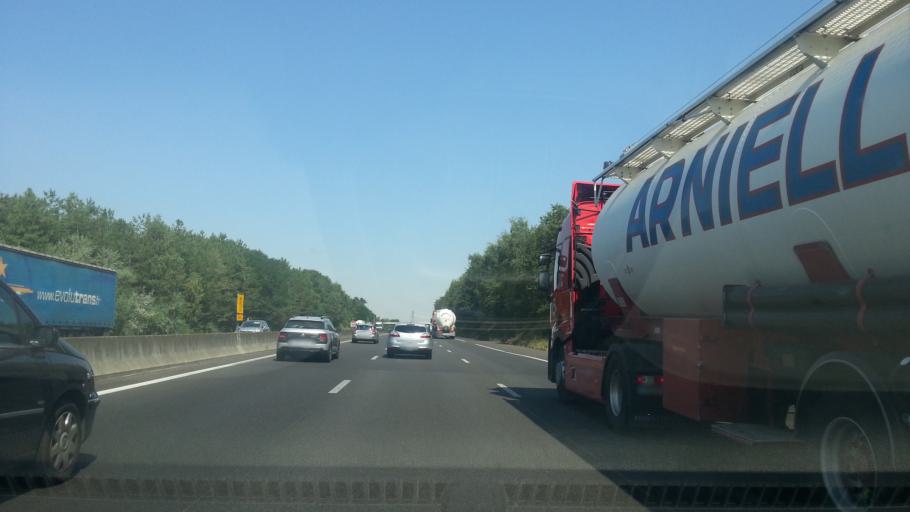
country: FR
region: Centre
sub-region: Departement du Loiret
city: Ingre
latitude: 47.9349
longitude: 1.8492
